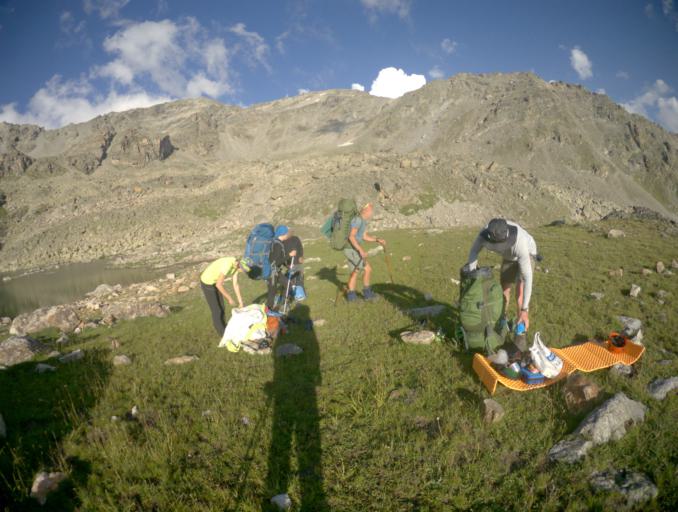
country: RU
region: Karachayevo-Cherkesiya
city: Uchkulan
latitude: 43.3129
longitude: 42.0674
